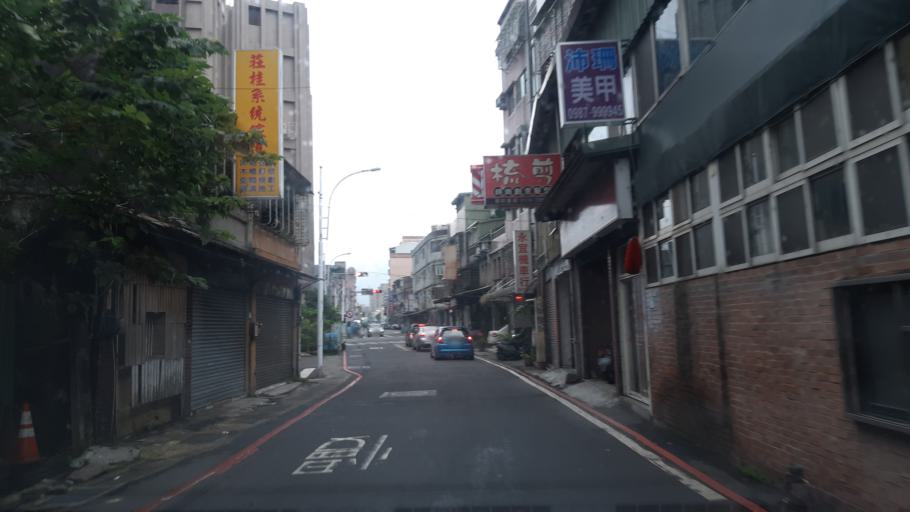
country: TW
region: Taiwan
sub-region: Taoyuan
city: Taoyuan
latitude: 24.9278
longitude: 121.3687
